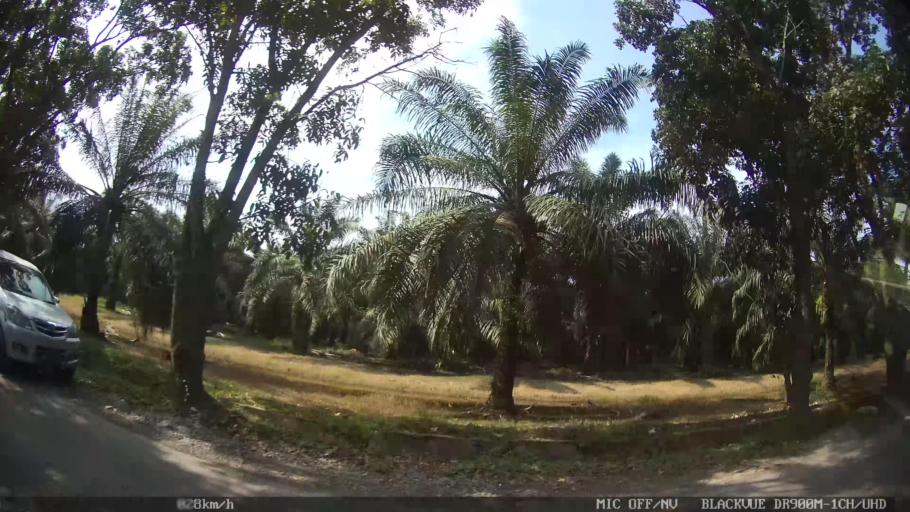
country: ID
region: North Sumatra
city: Binjai
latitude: 3.6511
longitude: 98.5272
